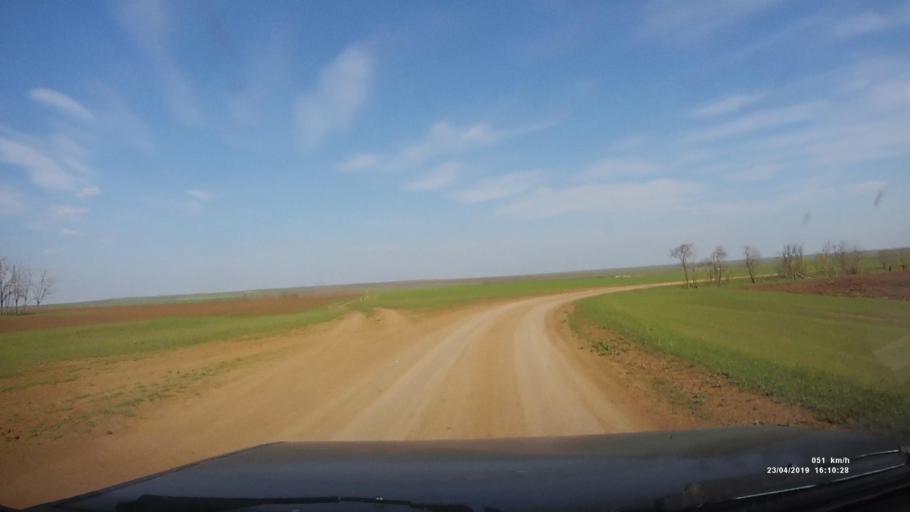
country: RU
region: Rostov
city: Remontnoye
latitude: 46.4814
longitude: 43.1223
